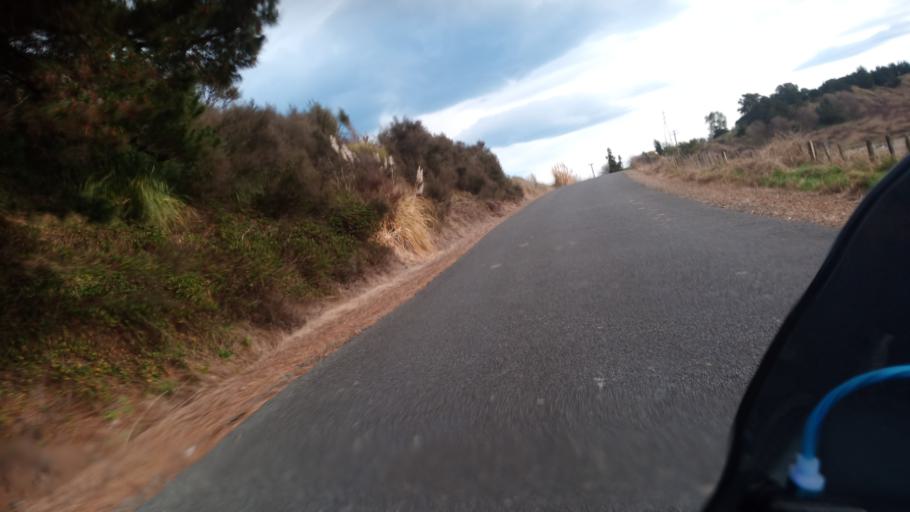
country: NZ
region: Hawke's Bay
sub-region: Wairoa District
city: Wairoa
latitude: -38.9729
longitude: 177.4351
